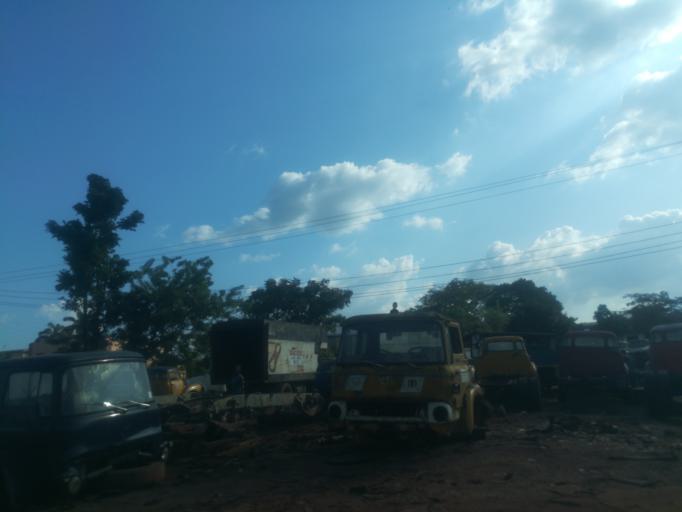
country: NG
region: Oyo
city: Egbeda
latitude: 7.3869
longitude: 3.9803
